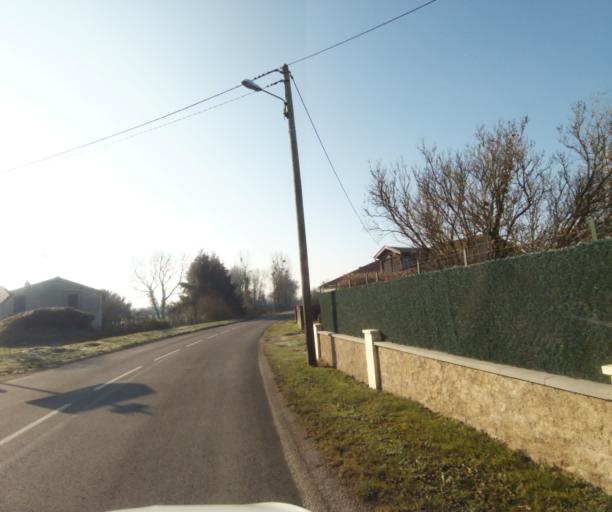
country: FR
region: Champagne-Ardenne
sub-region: Departement de la Haute-Marne
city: Montier-en-Der
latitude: 48.4530
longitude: 4.7678
